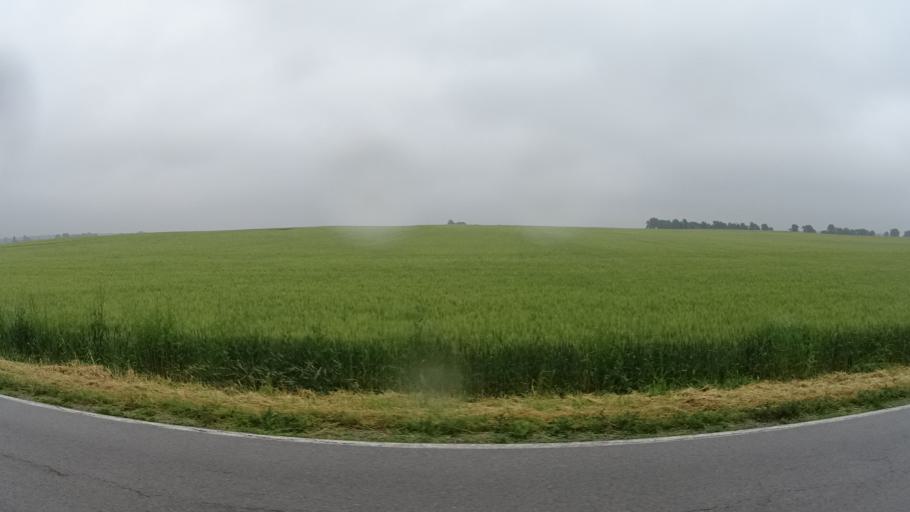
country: US
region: Ohio
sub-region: Huron County
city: Bellevue
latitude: 41.3119
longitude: -82.8424
